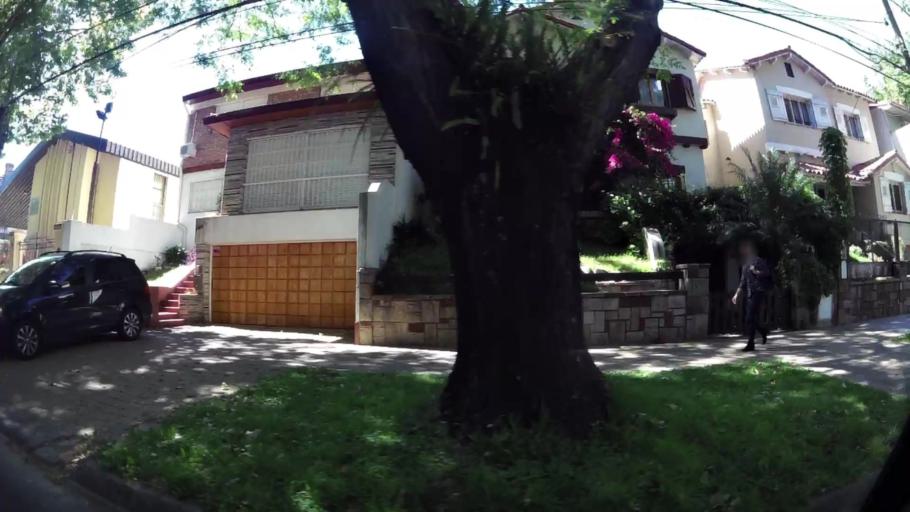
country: AR
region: Buenos Aires
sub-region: Partido de Vicente Lopez
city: Olivos
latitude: -34.5205
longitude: -58.4843
